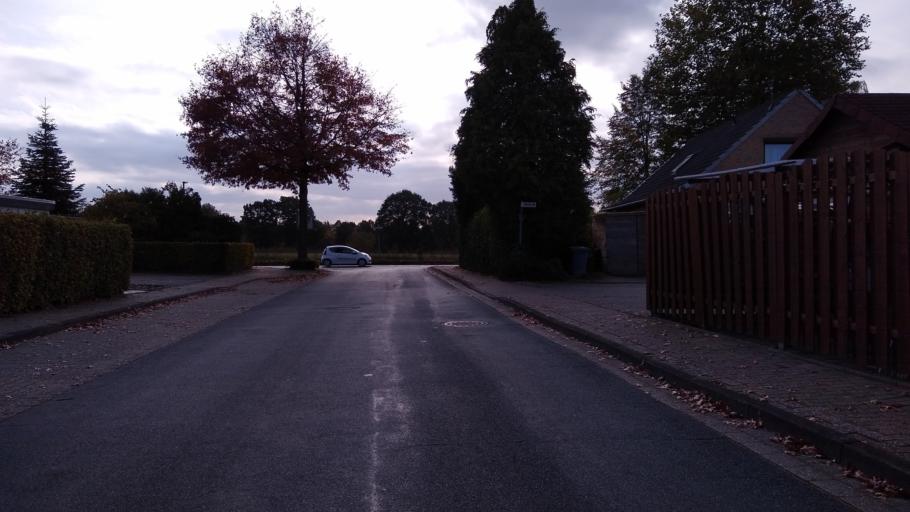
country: DE
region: Lower Saxony
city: Rastede
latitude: 53.2036
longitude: 8.2388
